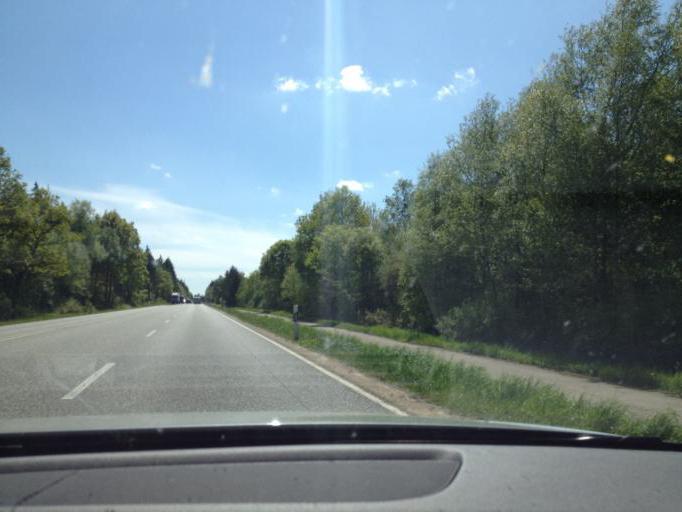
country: DE
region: Rheinland-Pfalz
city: Kerschenbach
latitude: 50.3314
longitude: 6.5139
